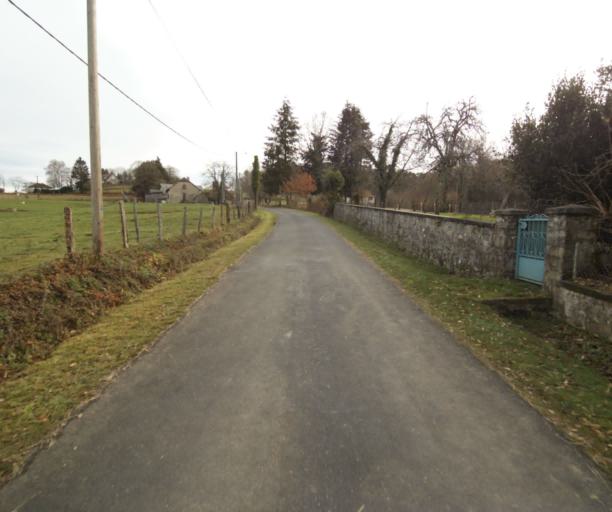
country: FR
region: Limousin
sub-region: Departement de la Correze
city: Saint-Mexant
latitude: 45.2806
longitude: 1.6783
